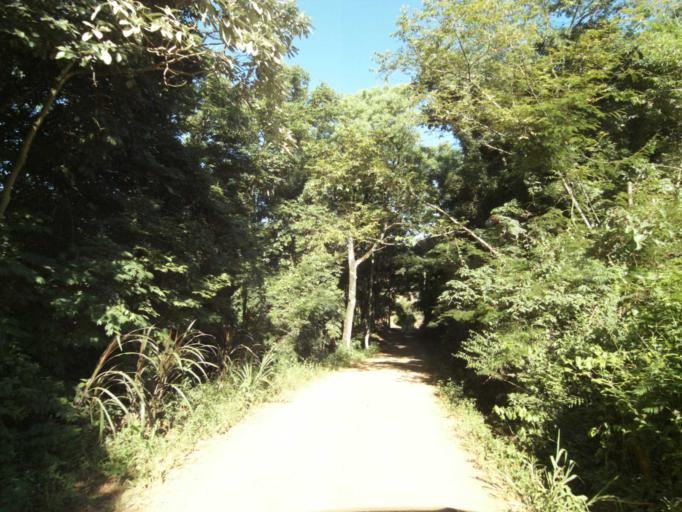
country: BR
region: Parana
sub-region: Francisco Beltrao
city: Francisco Beltrao
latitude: -26.1418
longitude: -53.3122
